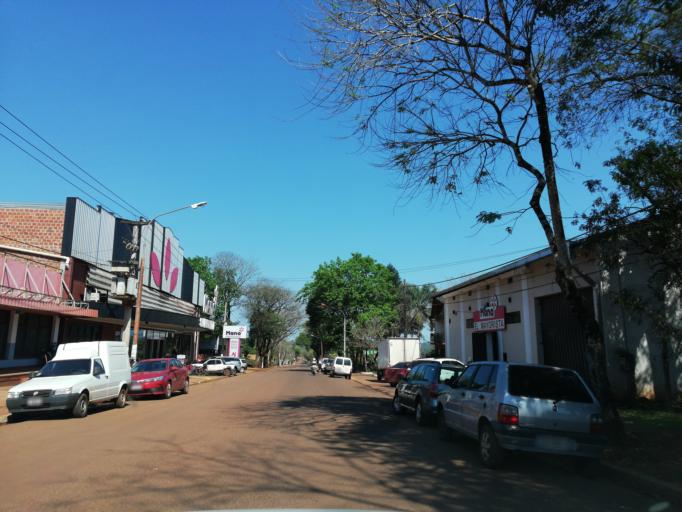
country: AR
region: Misiones
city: Puerto Eldorado
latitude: -26.4089
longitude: -54.6741
